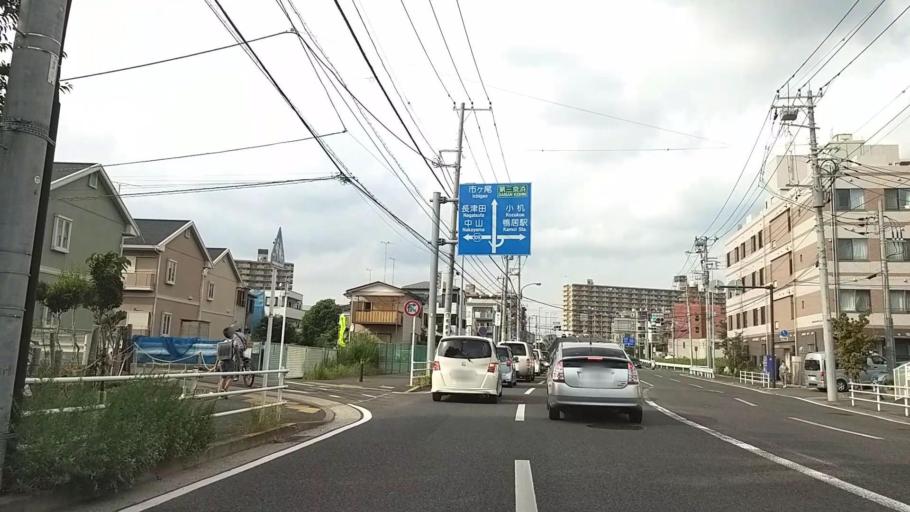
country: JP
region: Kanagawa
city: Yokohama
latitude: 35.5076
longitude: 139.5640
